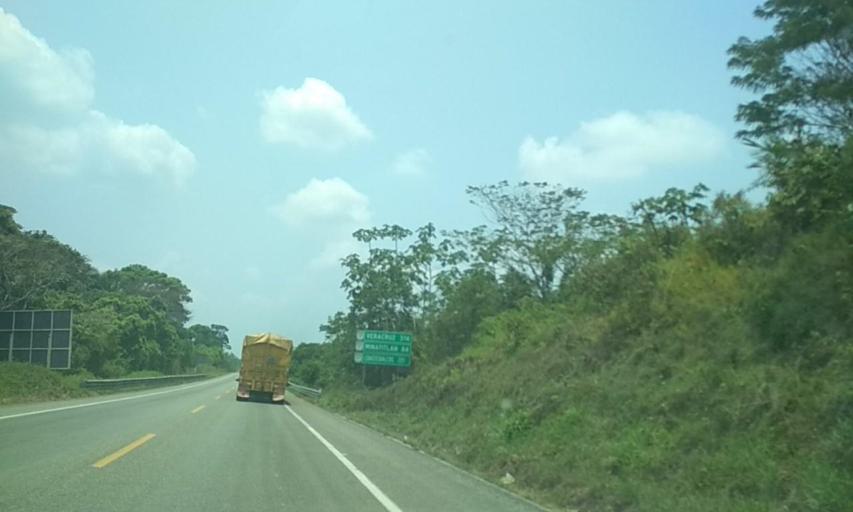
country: MX
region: Tabasco
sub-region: Huimanguillo
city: Francisco Rueda
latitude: 17.7293
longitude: -93.9659
